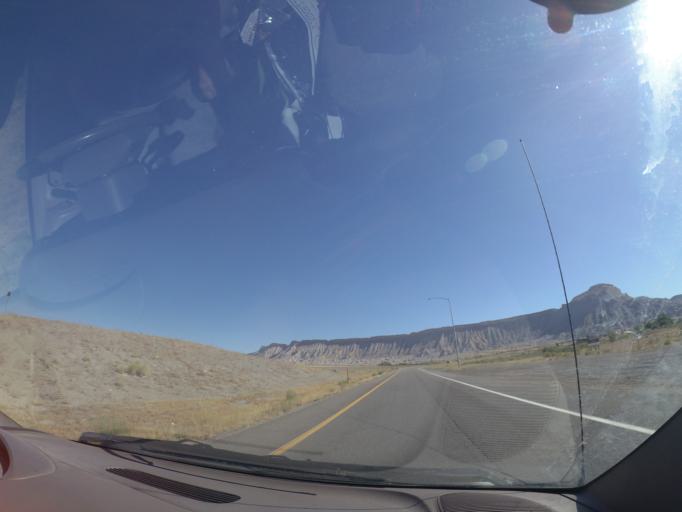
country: US
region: Colorado
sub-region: Mesa County
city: Clifton
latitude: 39.1023
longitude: -108.4463
